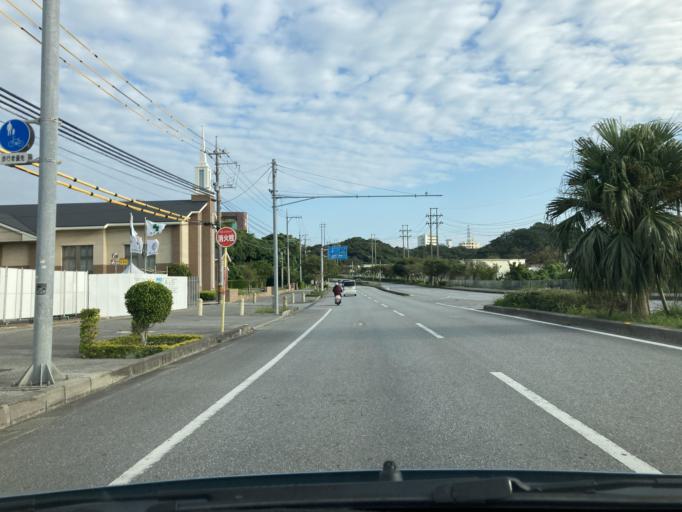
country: JP
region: Okinawa
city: Okinawa
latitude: 26.3582
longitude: 127.8012
